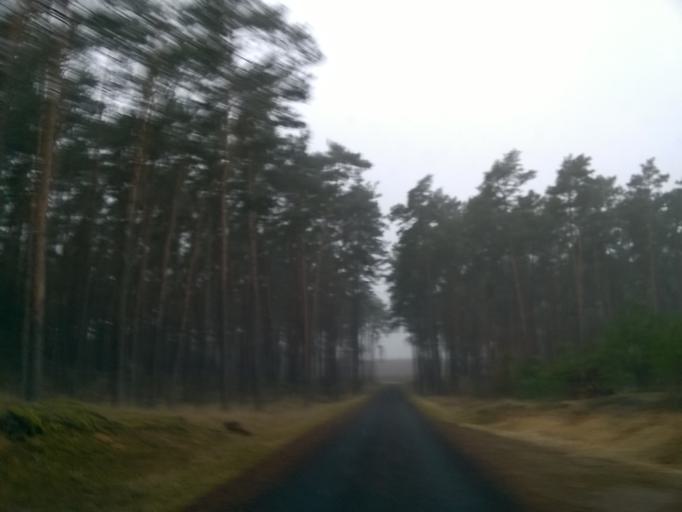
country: PL
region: Kujawsko-Pomorskie
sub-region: Powiat nakielski
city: Kcynia
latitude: 53.0535
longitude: 17.4512
